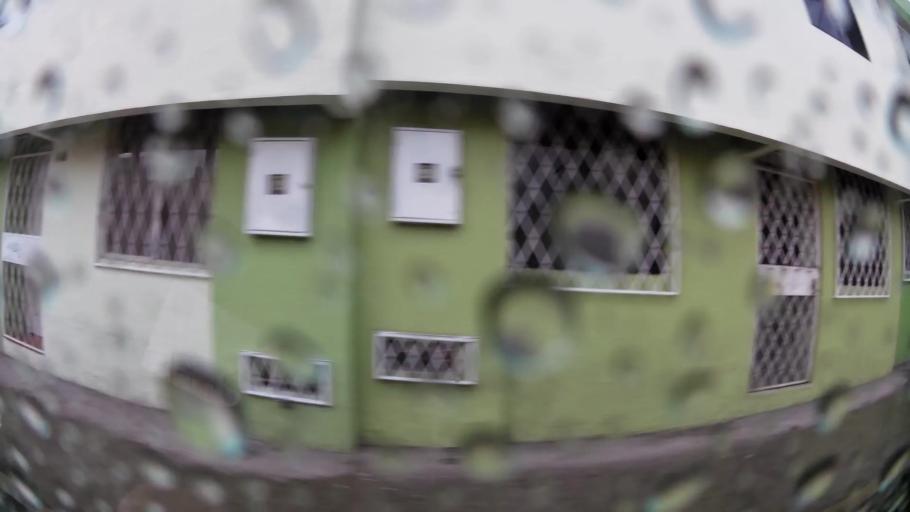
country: EC
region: Pichincha
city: Quito
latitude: -0.3050
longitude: -78.5480
